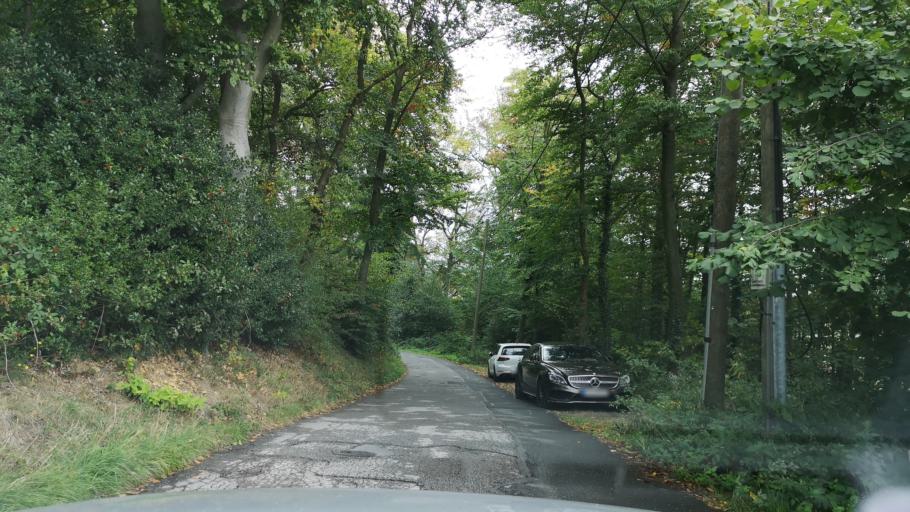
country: DE
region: North Rhine-Westphalia
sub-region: Regierungsbezirk Dusseldorf
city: Velbert
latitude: 51.3722
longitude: 7.0193
